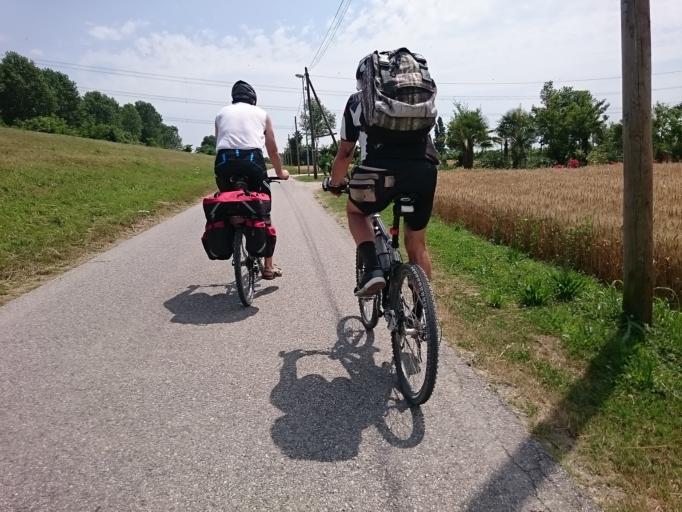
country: IT
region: Veneto
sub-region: Provincia di Padova
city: Codevigo
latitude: 45.2306
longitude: 12.1283
